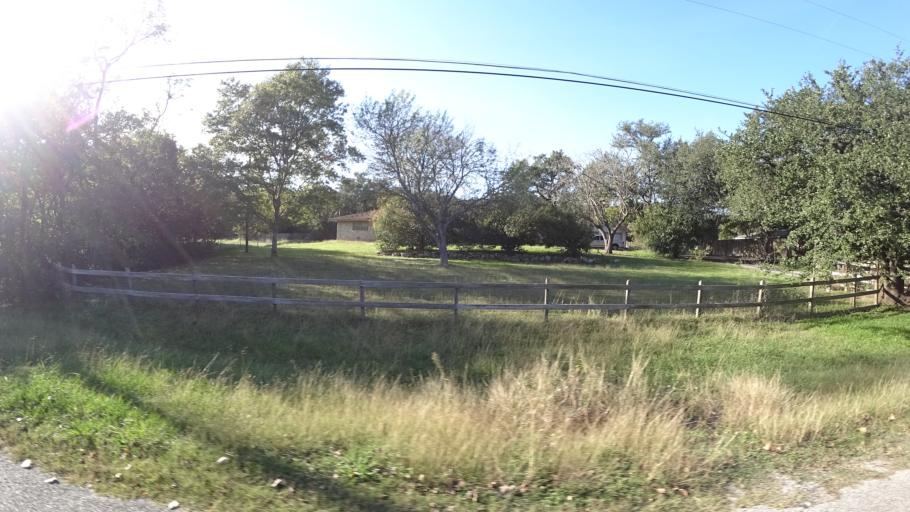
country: US
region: Texas
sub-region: Travis County
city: Barton Creek
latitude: 30.2426
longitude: -97.9154
